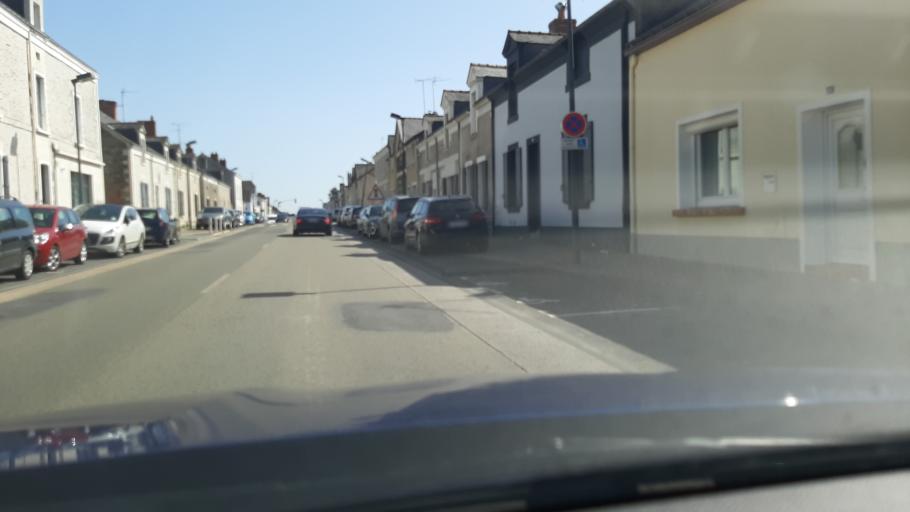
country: FR
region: Pays de la Loire
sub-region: Departement de Maine-et-Loire
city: Les Ponts-de-Ce
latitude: 47.4444
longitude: -0.5003
